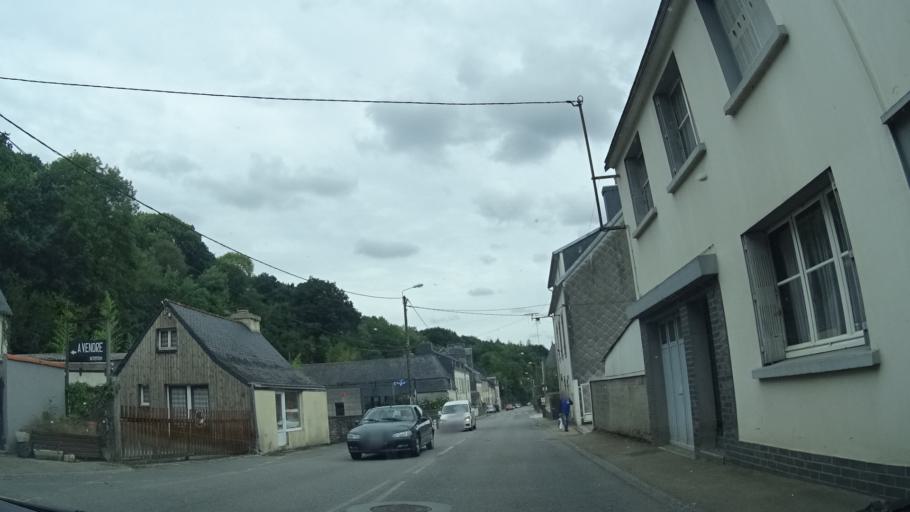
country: FR
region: Brittany
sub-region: Departement du Finistere
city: Chateaulin
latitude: 48.1975
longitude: -4.0982
